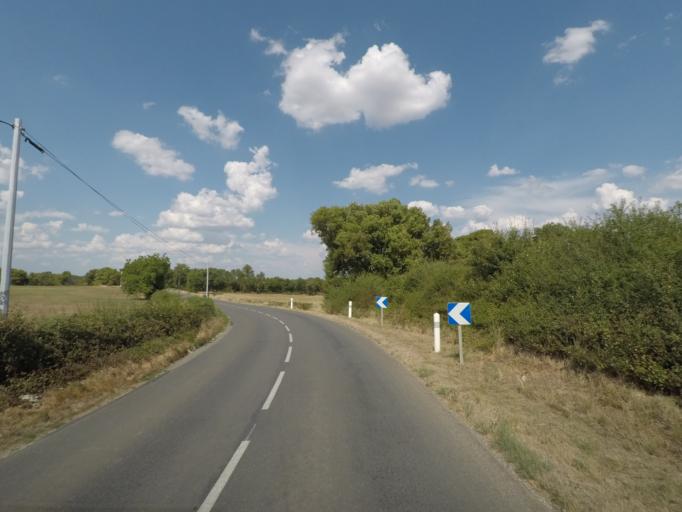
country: FR
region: Midi-Pyrenees
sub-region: Departement du Lot
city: Gramat
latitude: 44.6747
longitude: 1.6007
